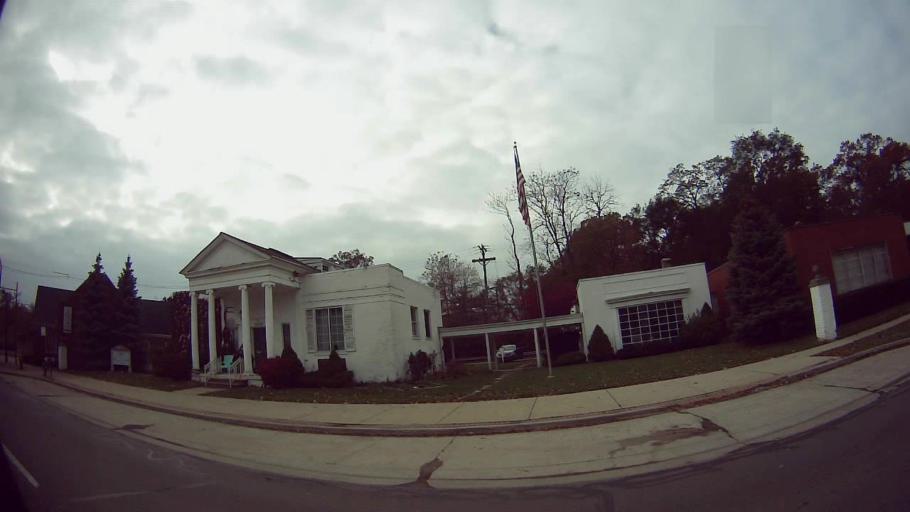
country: US
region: Michigan
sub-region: Oakland County
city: Pleasant Ridge
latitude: 42.4682
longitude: -83.1400
